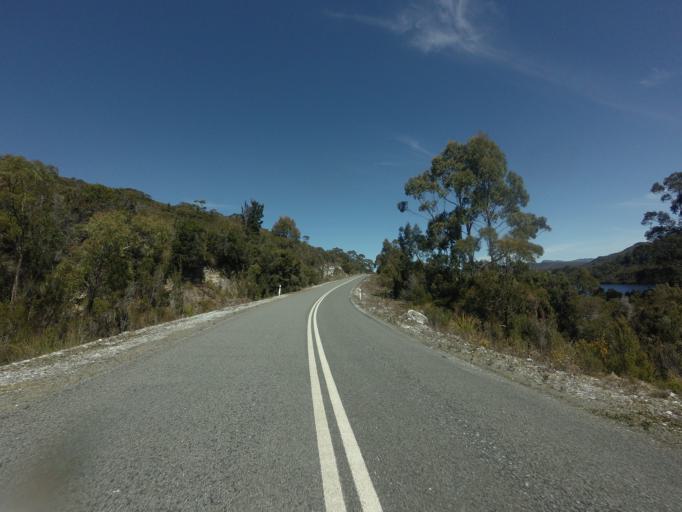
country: AU
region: Tasmania
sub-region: Huon Valley
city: Geeveston
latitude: -42.8229
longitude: 146.1248
